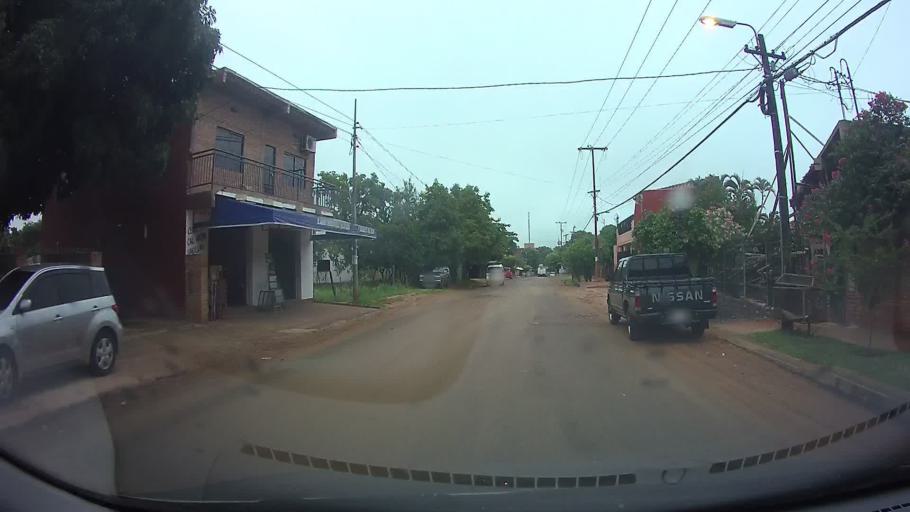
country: PY
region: Central
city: Itaugua
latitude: -25.3891
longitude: -57.3516
